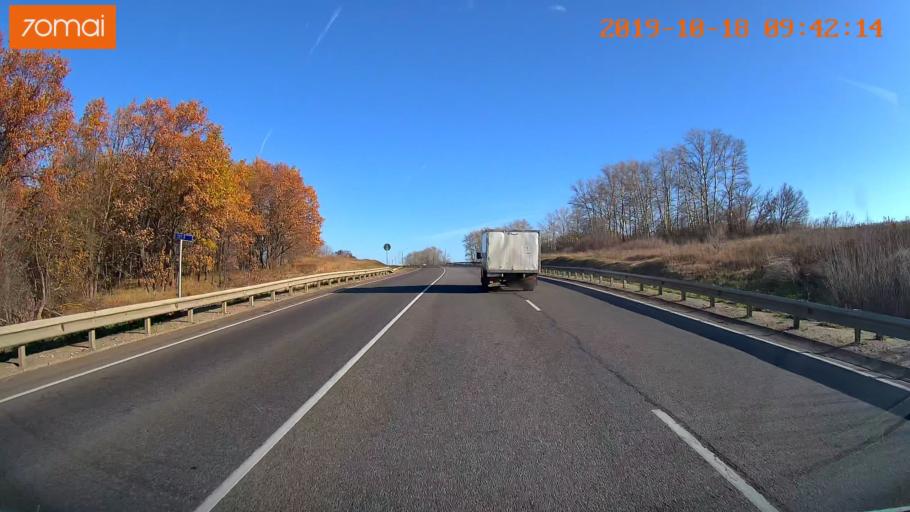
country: RU
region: Tula
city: Kazachka
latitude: 53.2848
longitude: 38.1740
